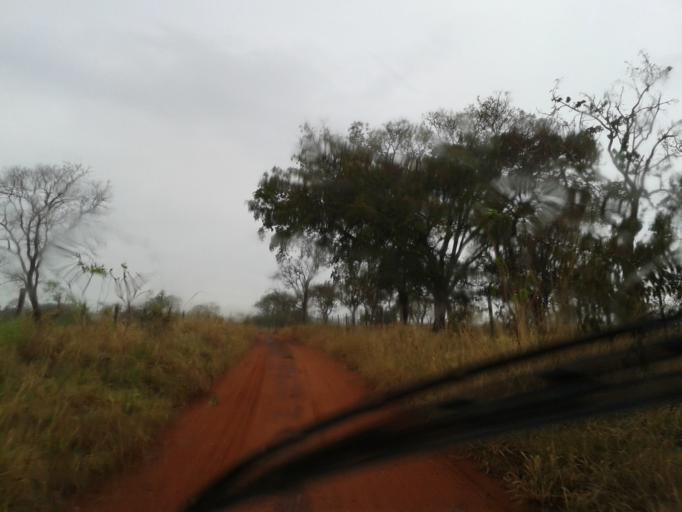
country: BR
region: Minas Gerais
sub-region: Campina Verde
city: Campina Verde
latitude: -19.3547
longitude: -49.5407
